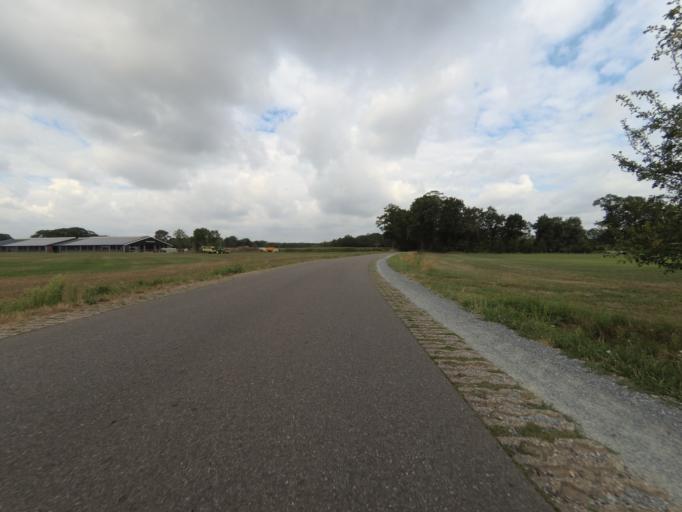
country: NL
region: Overijssel
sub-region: Gemeente Borne
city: Borne
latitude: 52.3138
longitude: 6.7789
